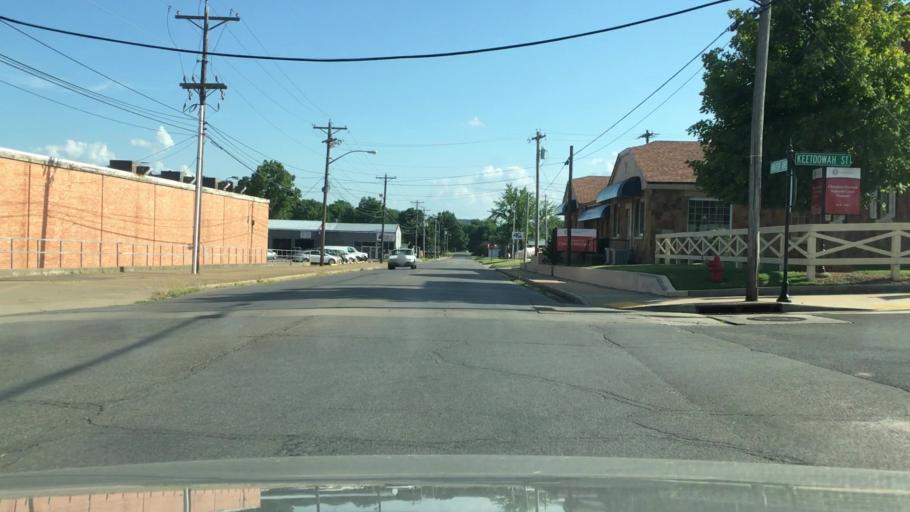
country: US
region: Oklahoma
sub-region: Cherokee County
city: Tahlequah
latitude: 35.9119
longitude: -94.9701
